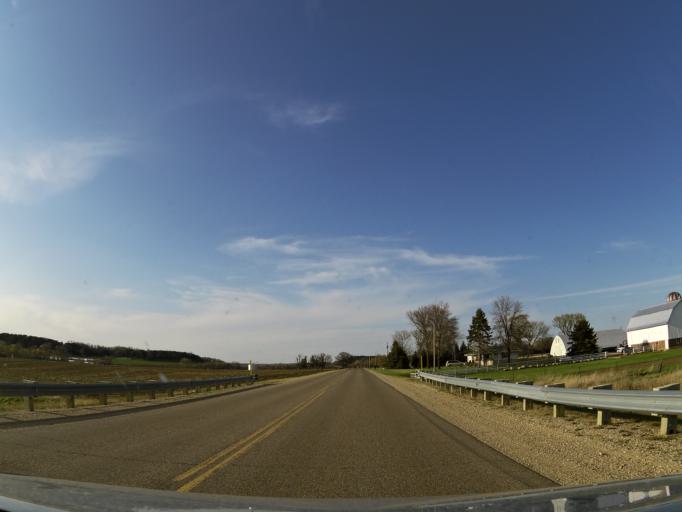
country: US
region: Wisconsin
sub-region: Pierce County
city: River Falls
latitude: 44.8146
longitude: -92.6447
